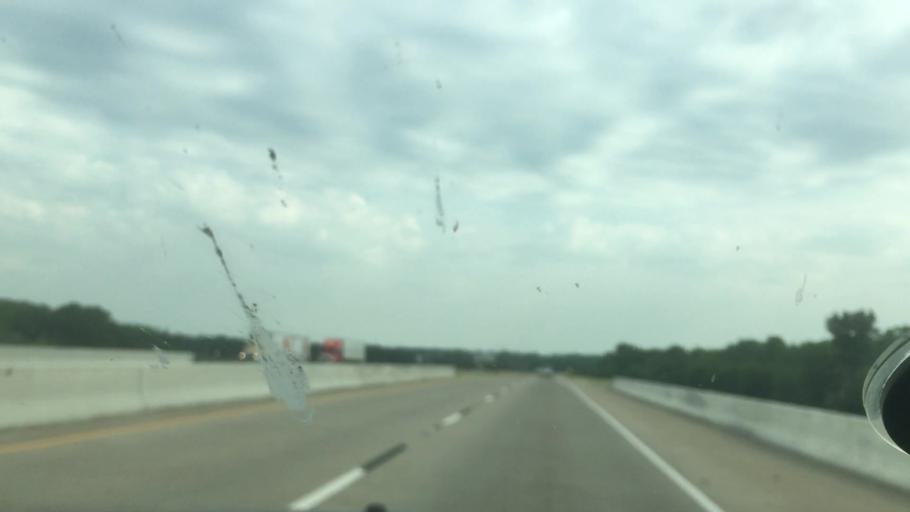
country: US
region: Oklahoma
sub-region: Bryan County
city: Colbert
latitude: 33.8098
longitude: -96.5346
